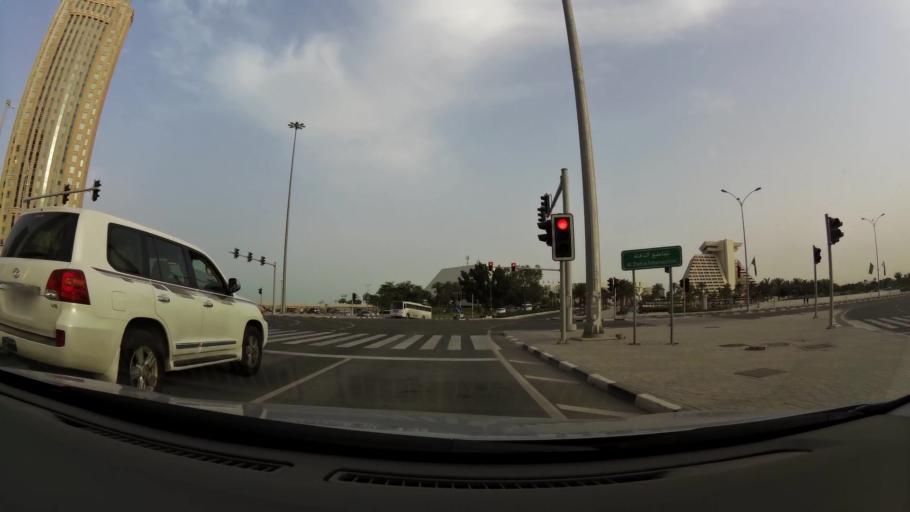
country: QA
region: Baladiyat ad Dawhah
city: Doha
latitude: 25.3231
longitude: 51.5358
